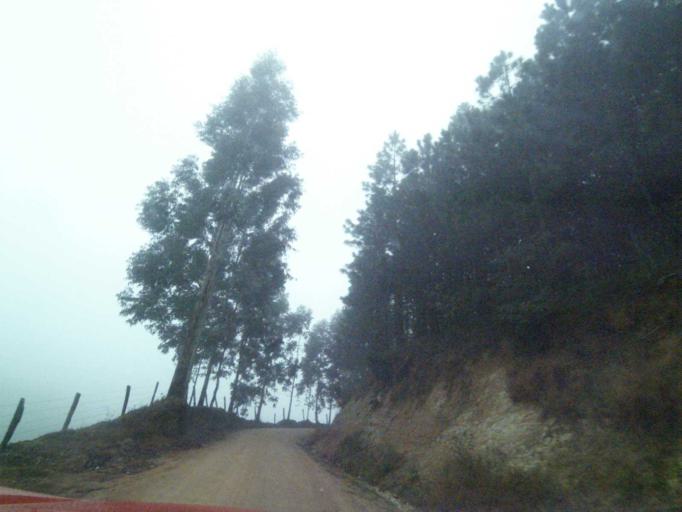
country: BR
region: Santa Catarina
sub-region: Anitapolis
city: Anitapolis
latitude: -27.9129
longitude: -49.1024
